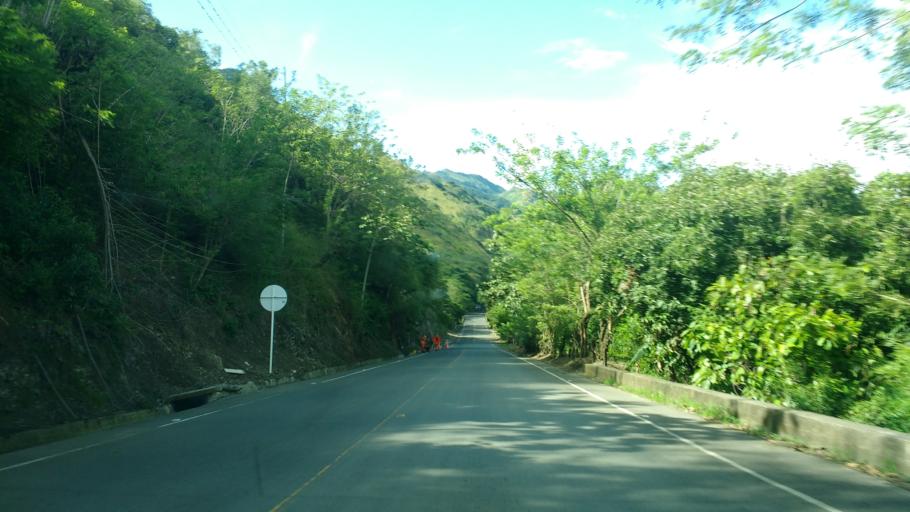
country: CO
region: Antioquia
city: Concordia
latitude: 6.0429
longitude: -75.8637
